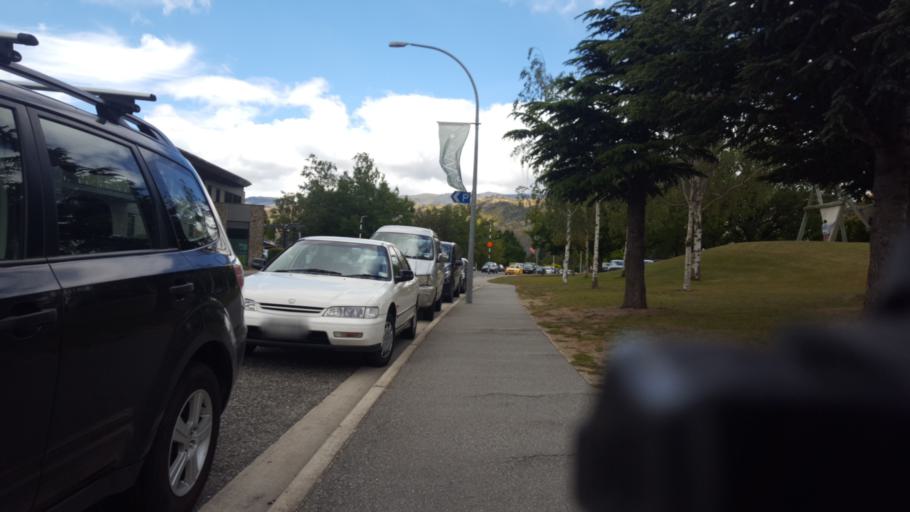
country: NZ
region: Otago
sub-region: Queenstown-Lakes District
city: Wanaka
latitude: -45.0380
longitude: 169.1955
